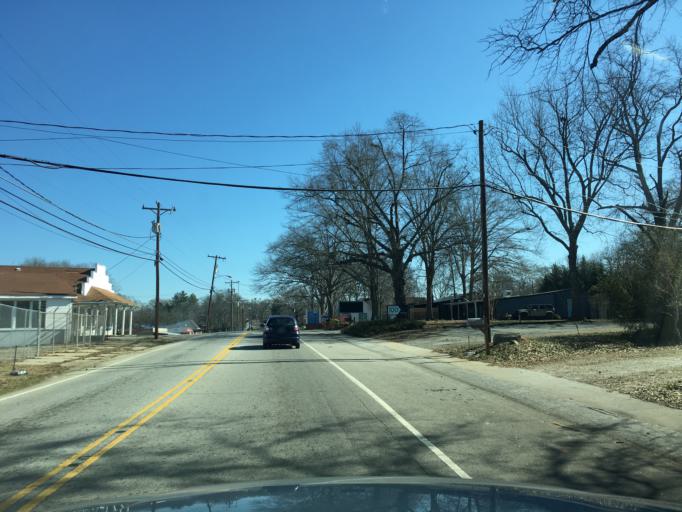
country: US
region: South Carolina
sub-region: Pickens County
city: Liberty
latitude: 34.7859
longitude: -82.6915
